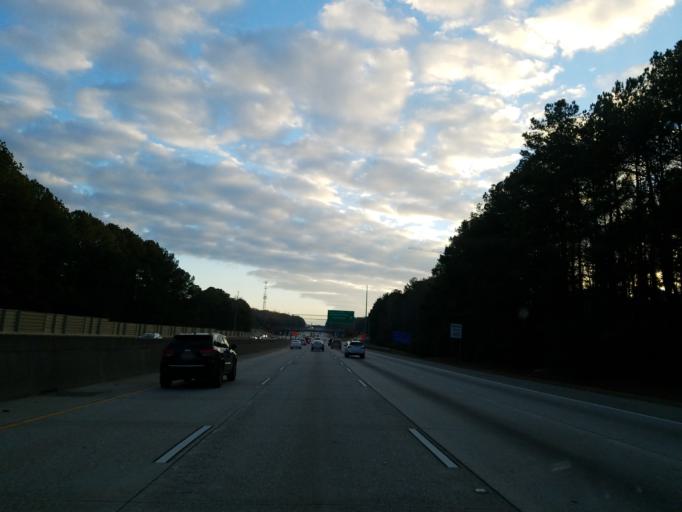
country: US
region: Georgia
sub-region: Fulton County
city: Alpharetta
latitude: 34.0738
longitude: -84.2693
